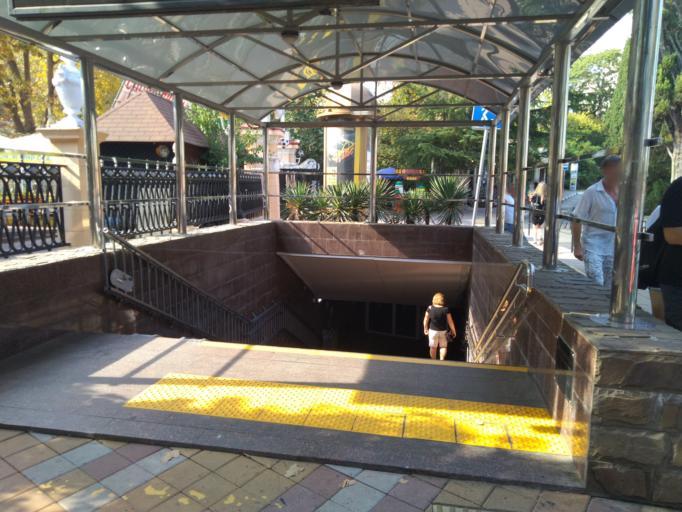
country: RU
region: Krasnodarskiy
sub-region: Sochi City
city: Sochi
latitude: 43.5933
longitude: 39.7175
